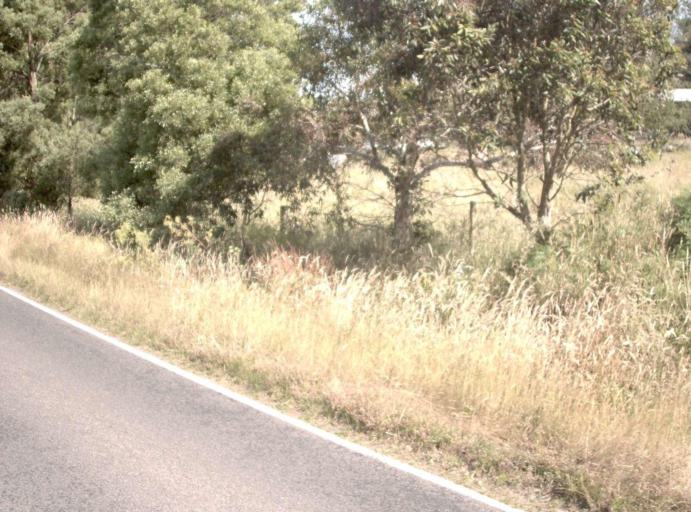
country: AU
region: Victoria
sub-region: Baw Baw
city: Warragul
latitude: -38.3566
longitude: 145.7919
